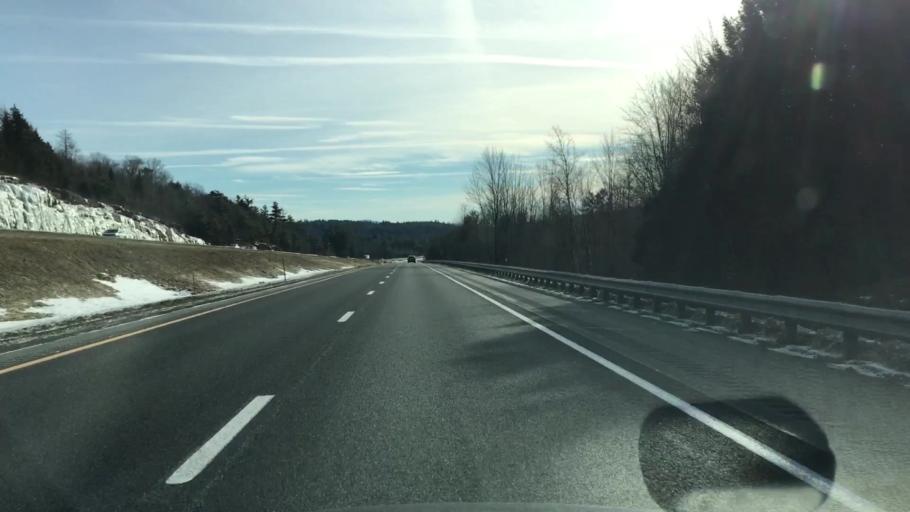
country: US
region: New Hampshire
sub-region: Sullivan County
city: Grantham
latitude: 43.5482
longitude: -72.1401
